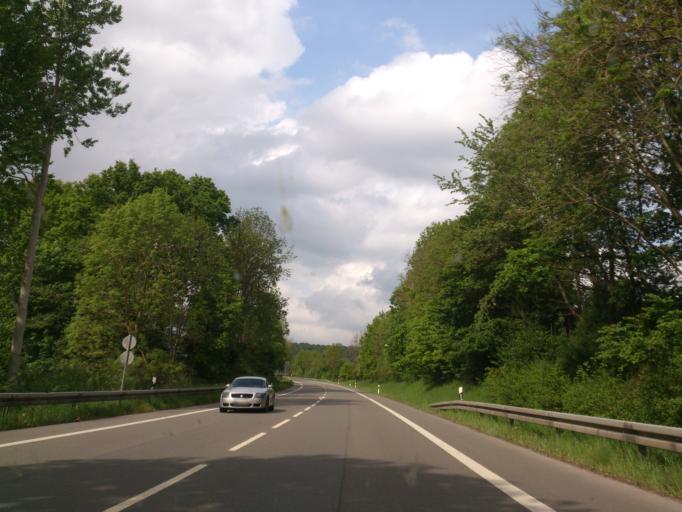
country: DE
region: Hesse
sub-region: Regierungsbezirk Kassel
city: Bad Arolsen
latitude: 51.4940
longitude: 9.0158
